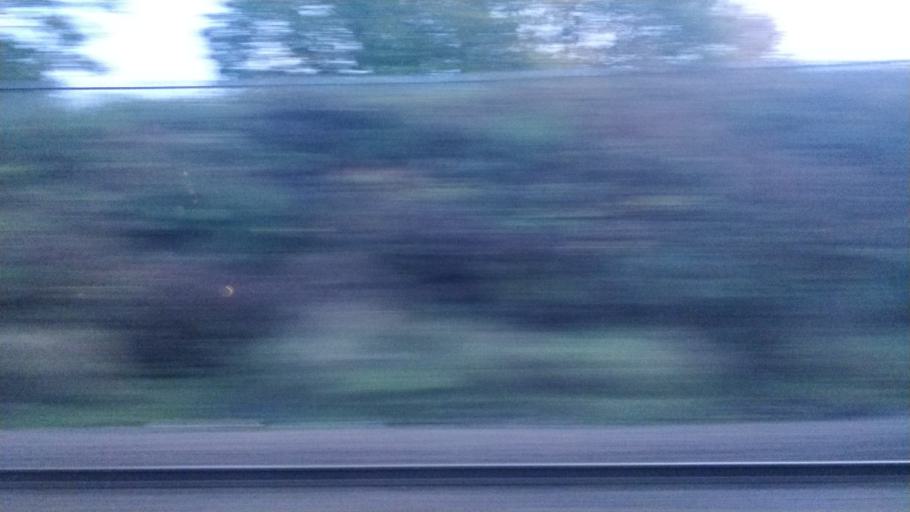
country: GB
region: England
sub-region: Borough of Bolton
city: Westhoughton
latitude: 53.5434
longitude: -2.5540
